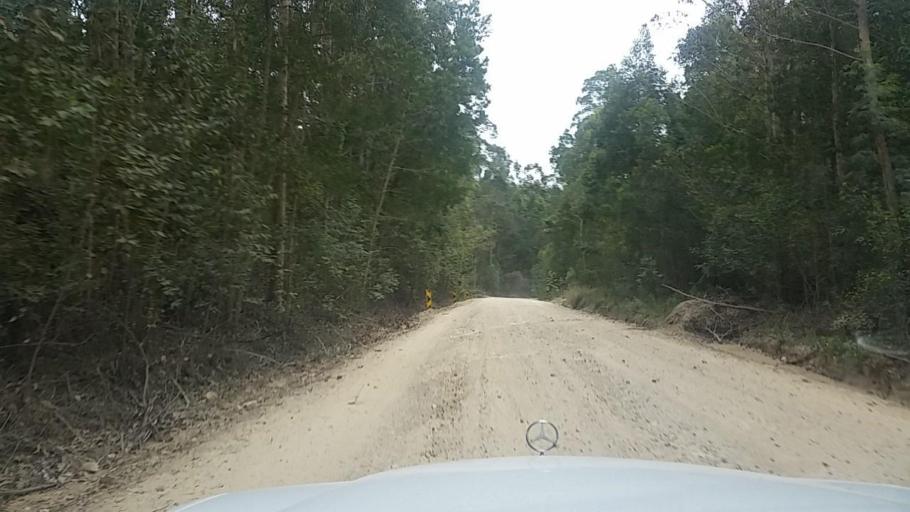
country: ZA
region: Western Cape
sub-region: Eden District Municipality
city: Knysna
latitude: -33.9972
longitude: 23.1281
